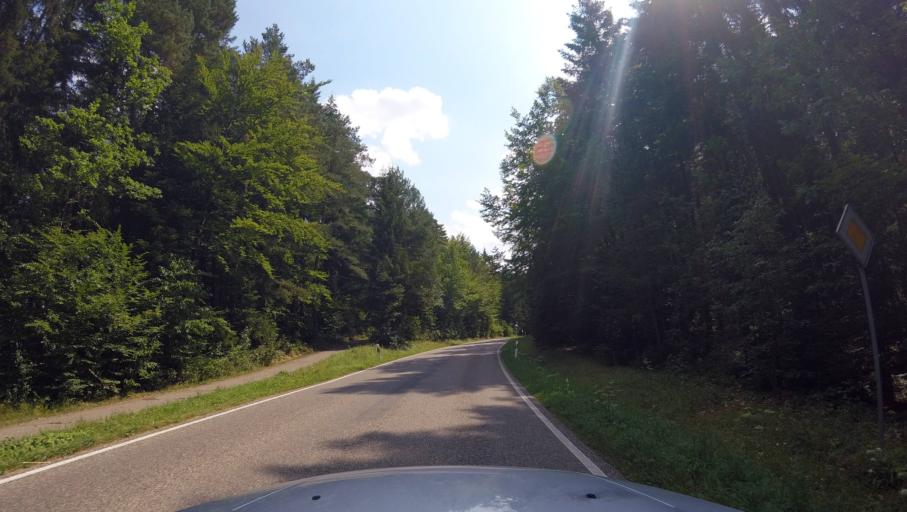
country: DE
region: Baden-Wuerttemberg
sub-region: Regierungsbezirk Stuttgart
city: Kaisersbach
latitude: 48.9099
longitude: 9.6902
